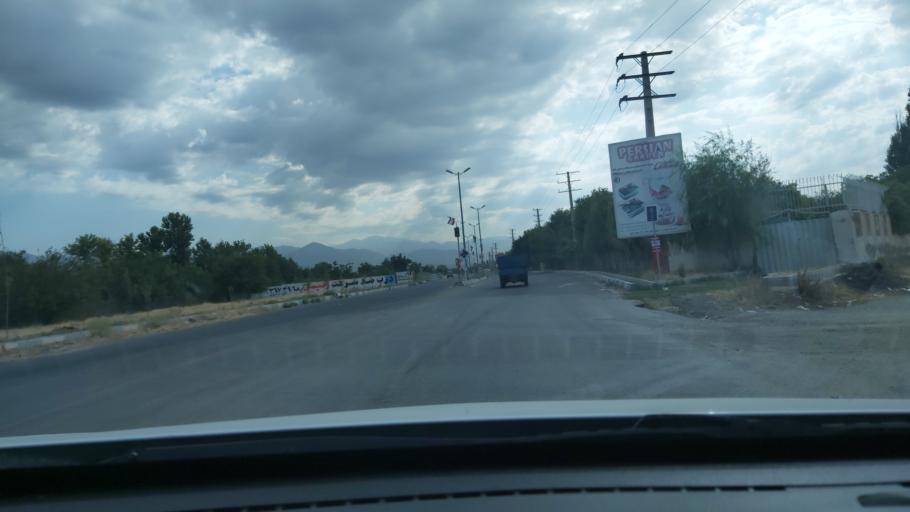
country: IR
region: Alborz
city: Hashtgerd
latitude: 35.9369
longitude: 50.7603
